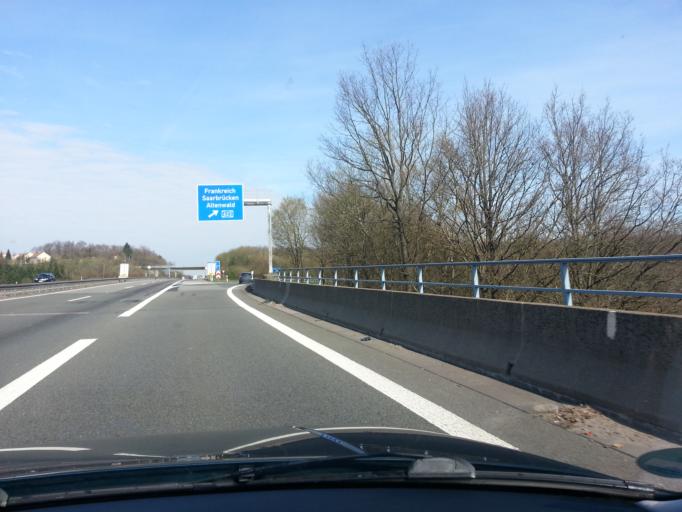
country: DE
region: Saarland
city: Friedrichsthal
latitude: 49.3180
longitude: 7.0834
